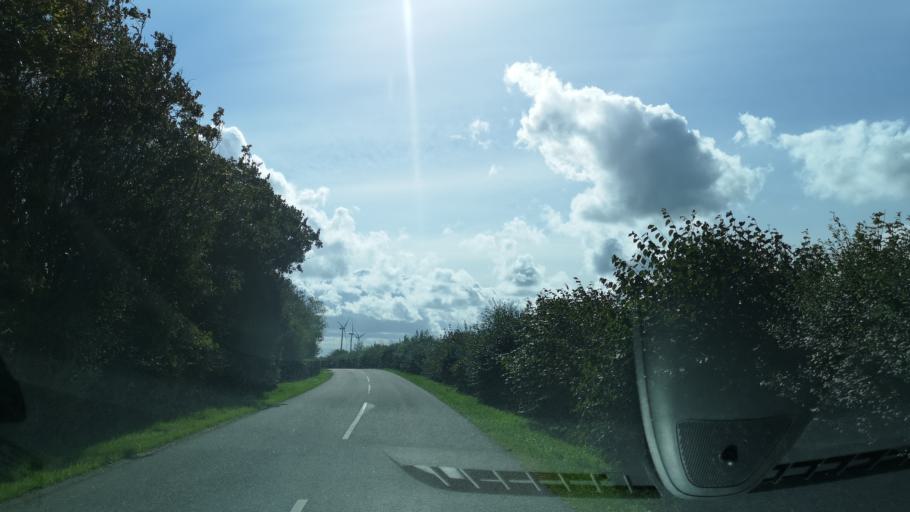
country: DK
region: Central Jutland
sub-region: Ringkobing-Skjern Kommune
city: Skjern
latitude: 55.9771
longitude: 8.5513
